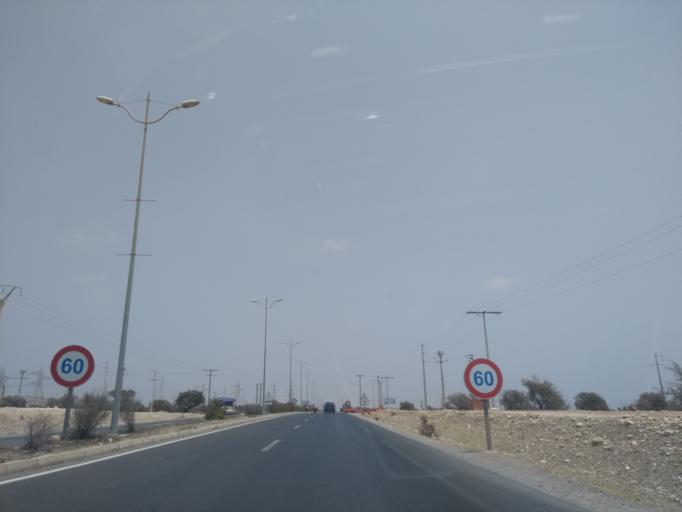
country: MA
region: Souss-Massa-Draa
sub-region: Inezgane-Ait Mellou
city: Inezgane
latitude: 30.3965
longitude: -9.4564
